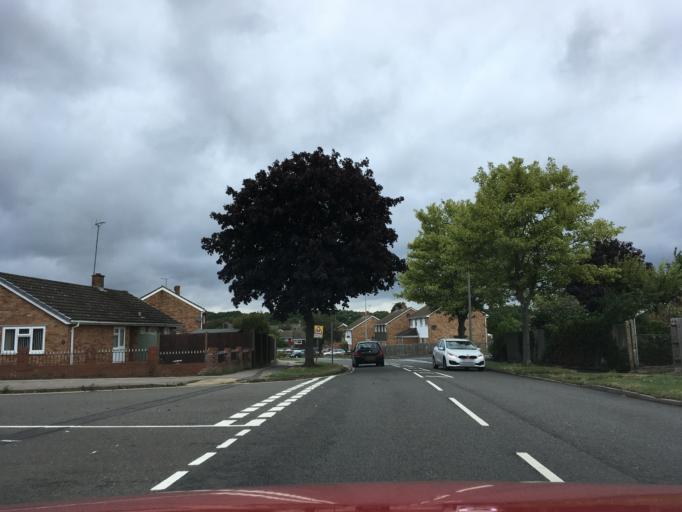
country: GB
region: England
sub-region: Buckinghamshire
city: Bletchley
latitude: 52.0068
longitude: -0.7435
